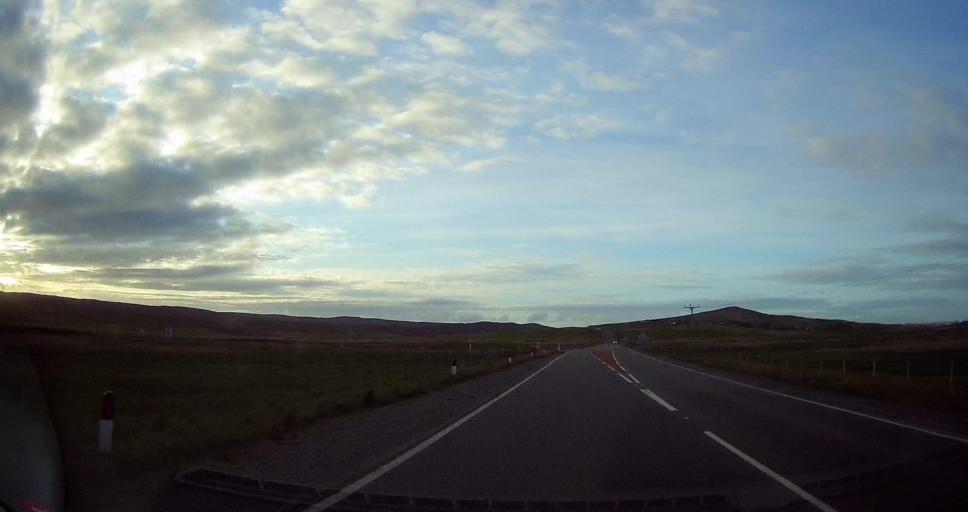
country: GB
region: Scotland
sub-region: Shetland Islands
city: Lerwick
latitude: 60.1898
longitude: -1.2321
